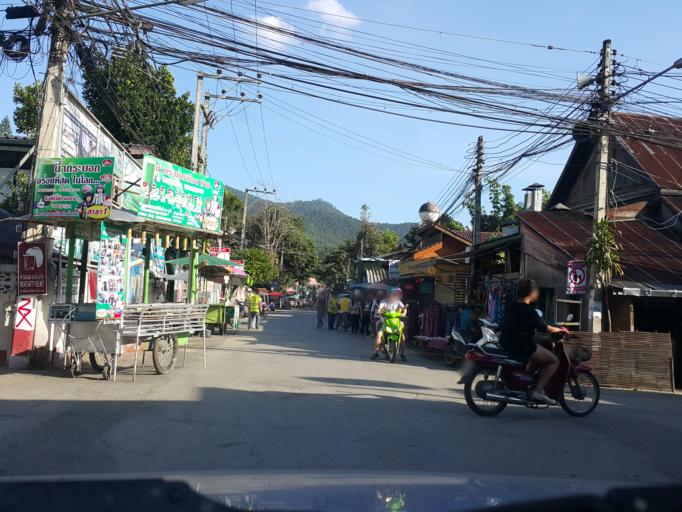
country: TH
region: Chiang Mai
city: Pai
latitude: 19.3601
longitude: 98.4415
